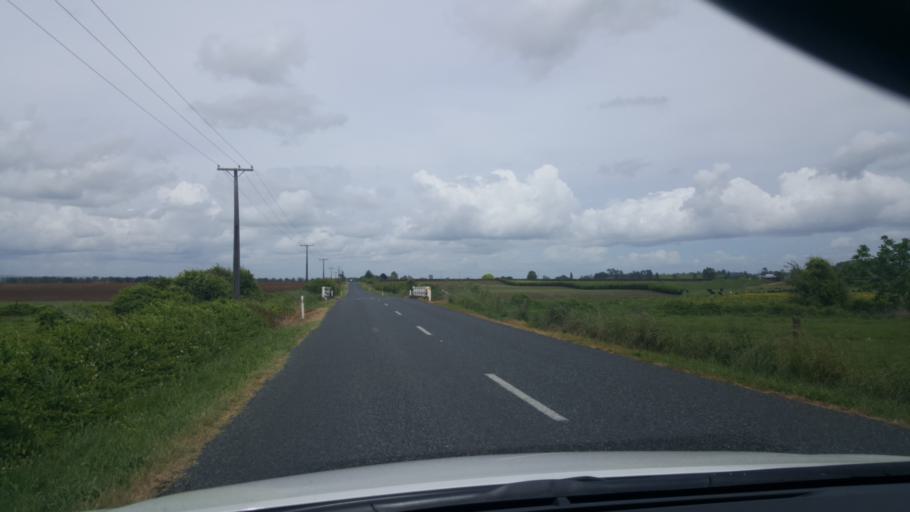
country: NZ
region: Waikato
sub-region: Matamata-Piako District
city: Matamata
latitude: -37.8753
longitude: 175.7262
